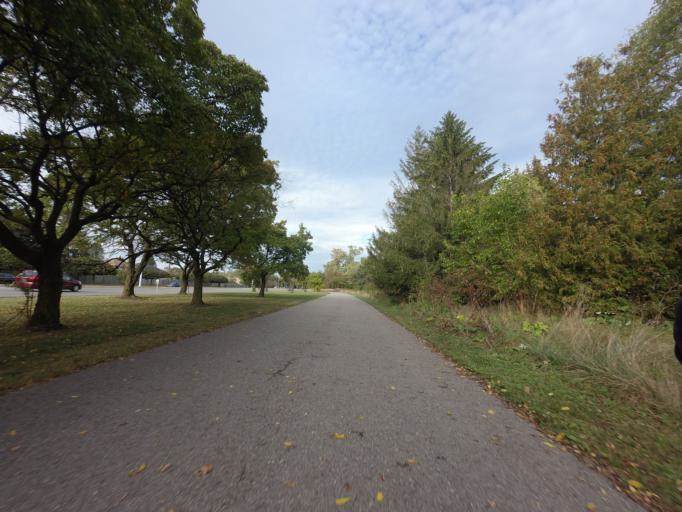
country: CA
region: Ontario
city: Mississauga
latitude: 43.5632
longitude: -79.6193
